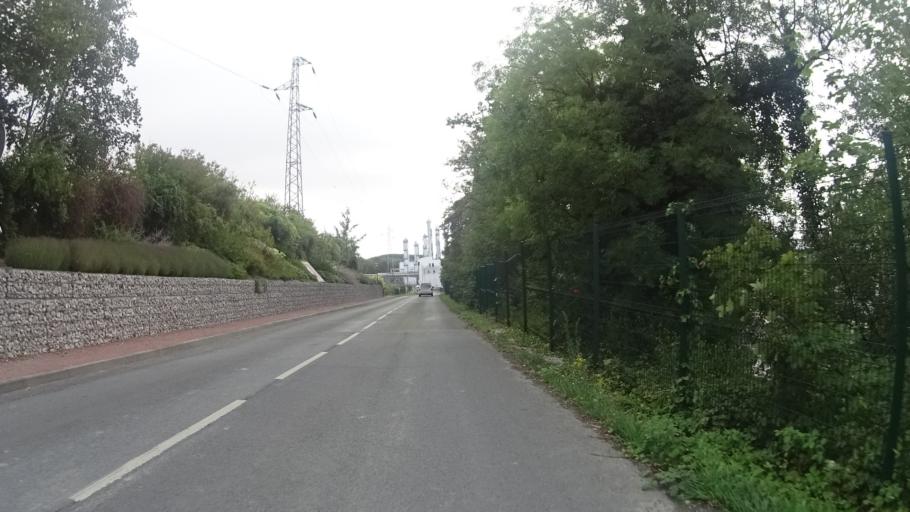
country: FR
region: Picardie
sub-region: Departement de l'Aisne
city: Origny-Sainte-Benoite
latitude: 49.8348
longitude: 3.4734
